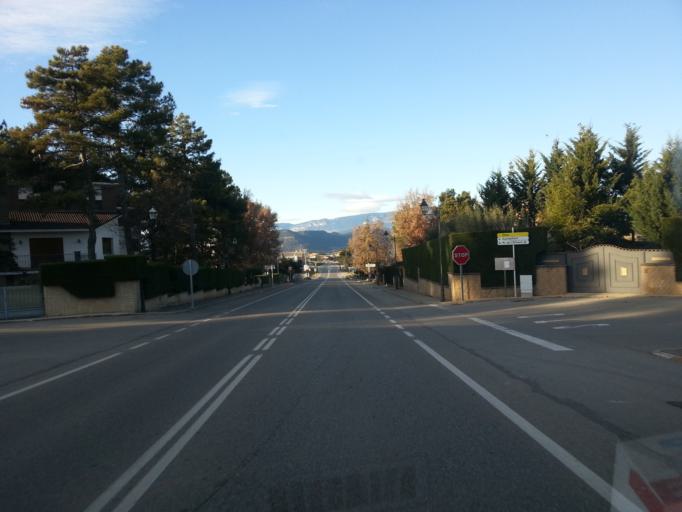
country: ES
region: Catalonia
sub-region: Provincia de Lleida
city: Olius
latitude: 41.9781
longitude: 1.5567
